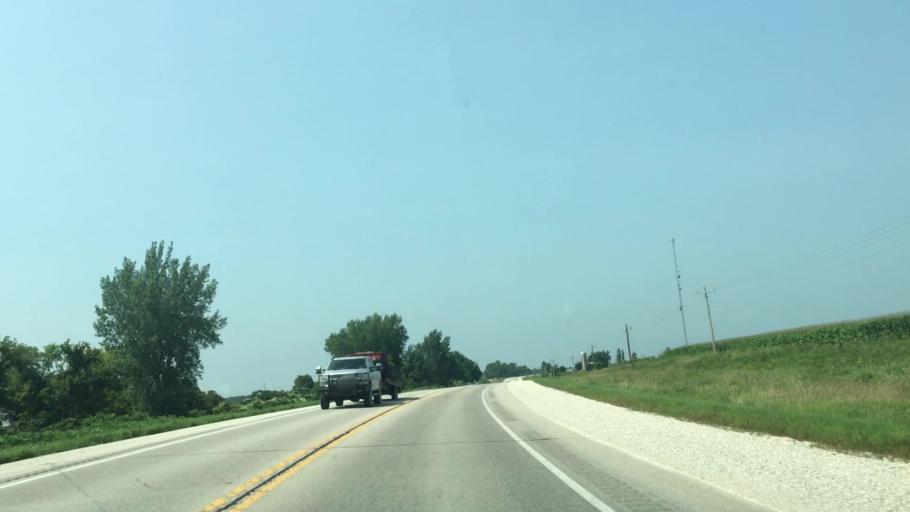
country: US
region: Iowa
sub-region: Winneshiek County
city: Decorah
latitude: 43.1955
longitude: -91.8732
